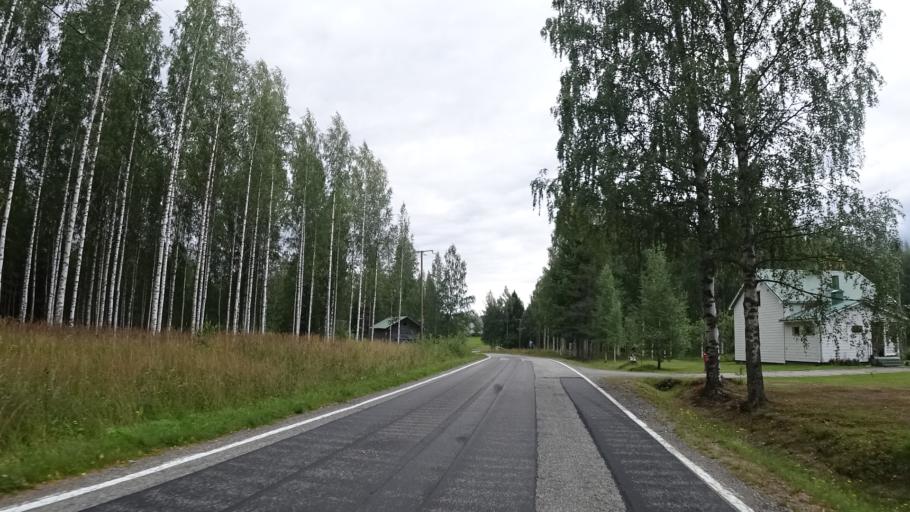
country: FI
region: North Karelia
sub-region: Joensuu
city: Ilomantsi
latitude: 62.4536
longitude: 31.1138
